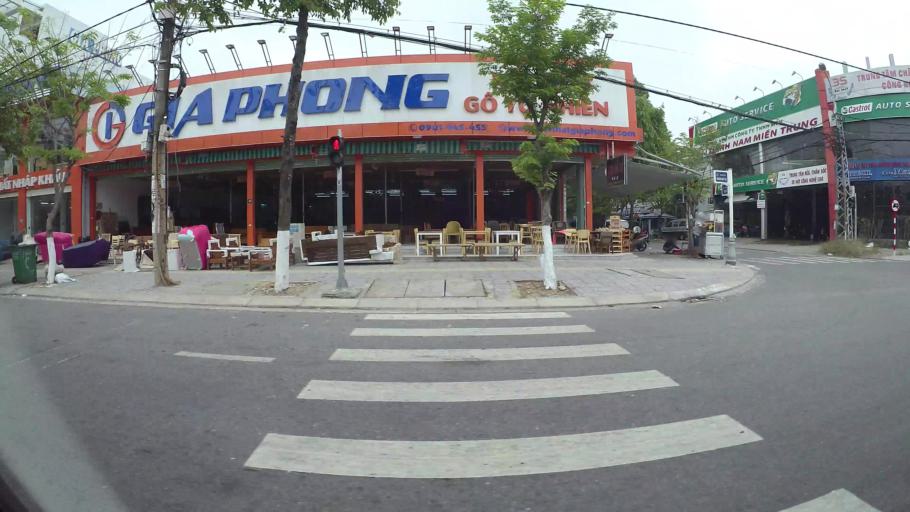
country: VN
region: Da Nang
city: Cam Le
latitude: 16.0340
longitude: 108.2093
